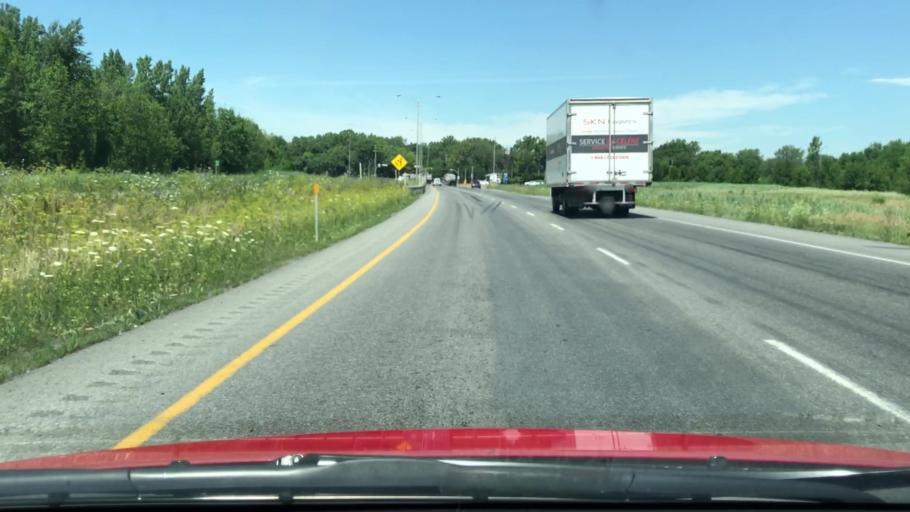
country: CA
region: Quebec
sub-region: Monteregie
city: Saint-Constant
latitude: 45.3923
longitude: -73.6036
